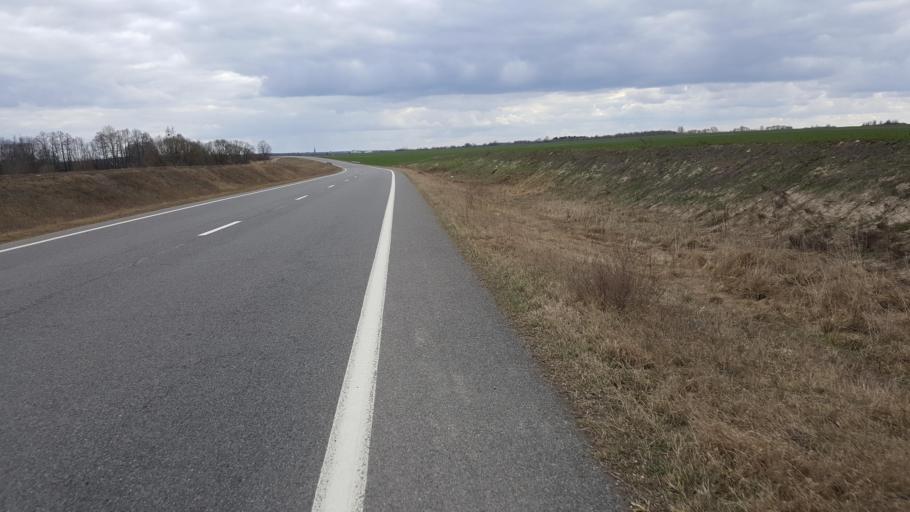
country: BY
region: Brest
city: Kamyanyets
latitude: 52.4410
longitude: 23.8314
